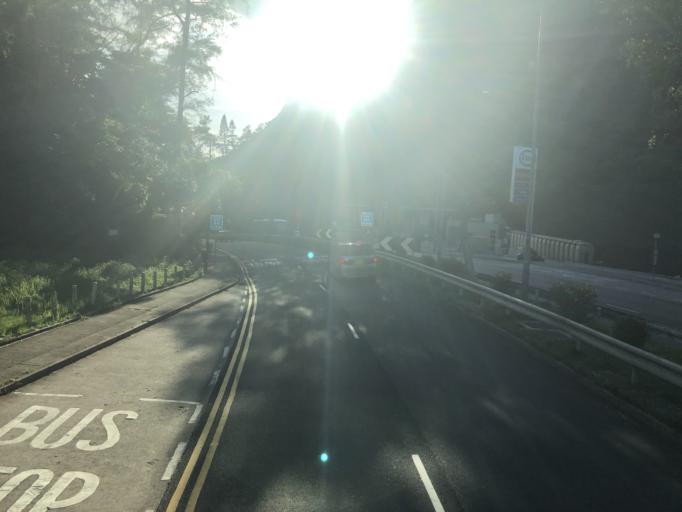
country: HK
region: Wong Tai Sin
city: Wong Tai Sin
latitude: 22.3345
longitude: 114.2307
